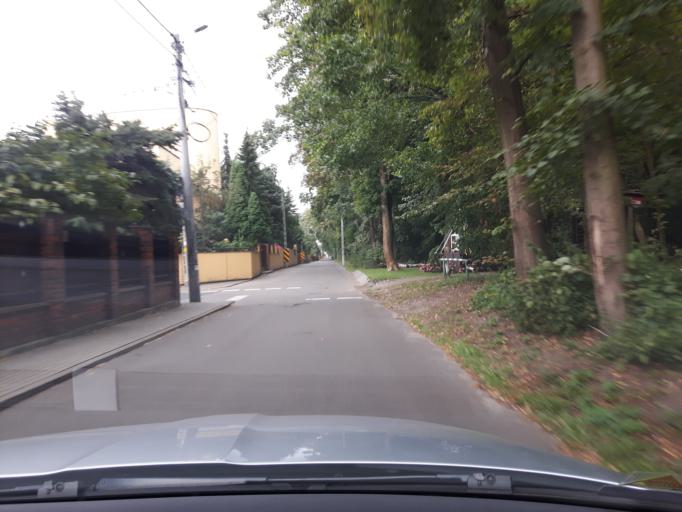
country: PL
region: Masovian Voivodeship
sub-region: Warszawa
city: Rembertow
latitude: 52.2487
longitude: 21.1255
